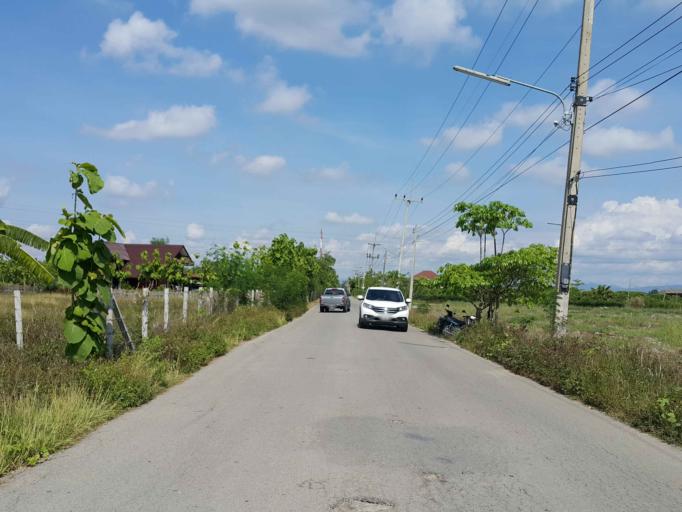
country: TH
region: Chiang Mai
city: San Kamphaeng
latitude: 18.7210
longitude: 99.0808
